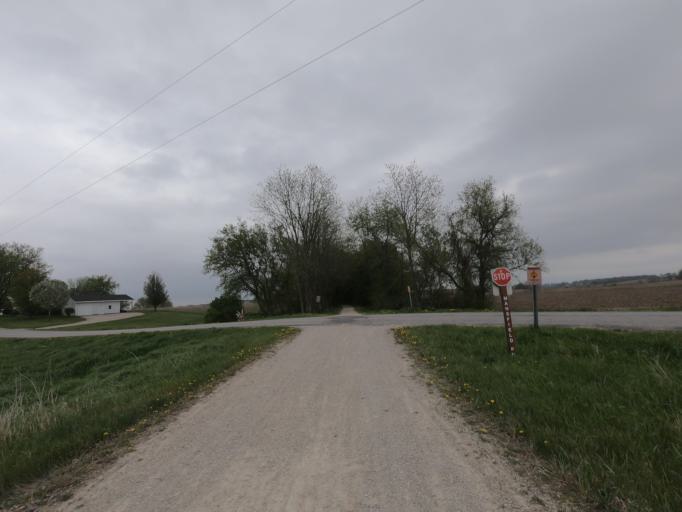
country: US
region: Wisconsin
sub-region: Jefferson County
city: Lake Mills
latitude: 43.0512
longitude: -88.8704
